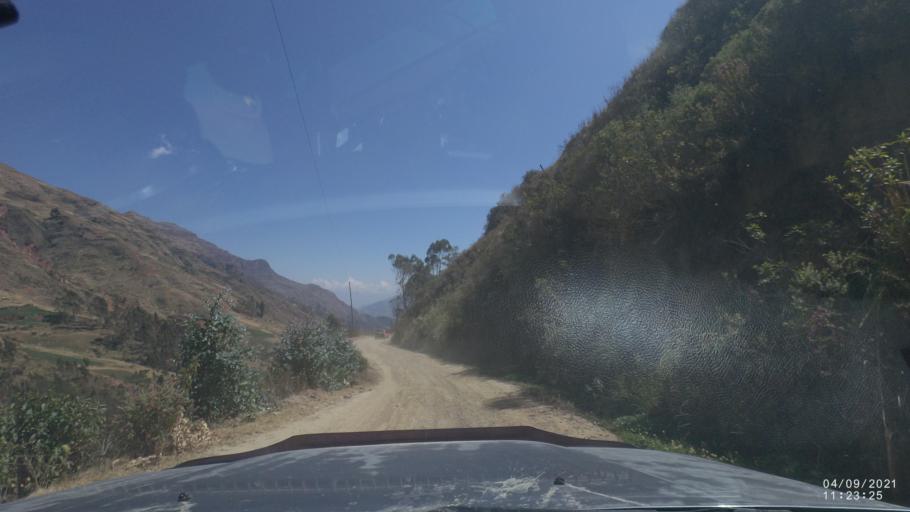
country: BO
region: Cochabamba
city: Colchani
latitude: -17.2636
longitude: -66.5067
